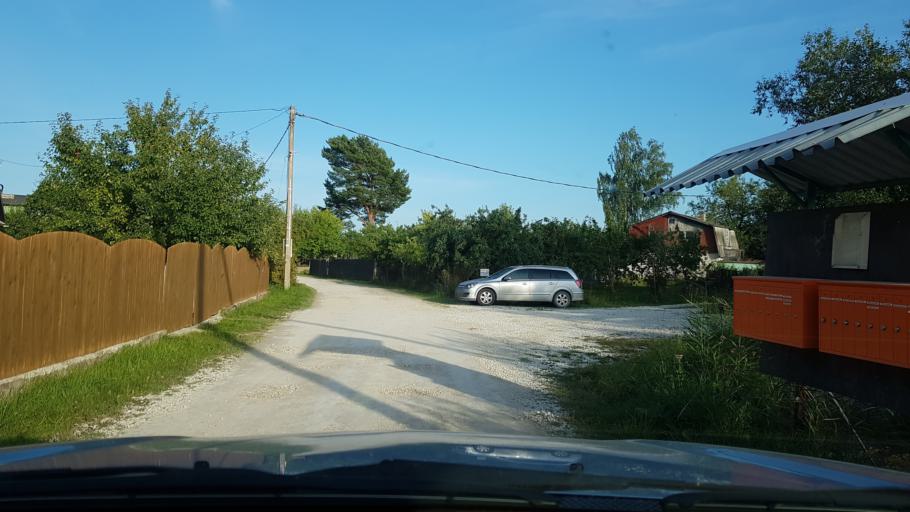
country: EE
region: Ida-Virumaa
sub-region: Sillamaee linn
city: Sillamae
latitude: 59.2588
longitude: 27.9266
